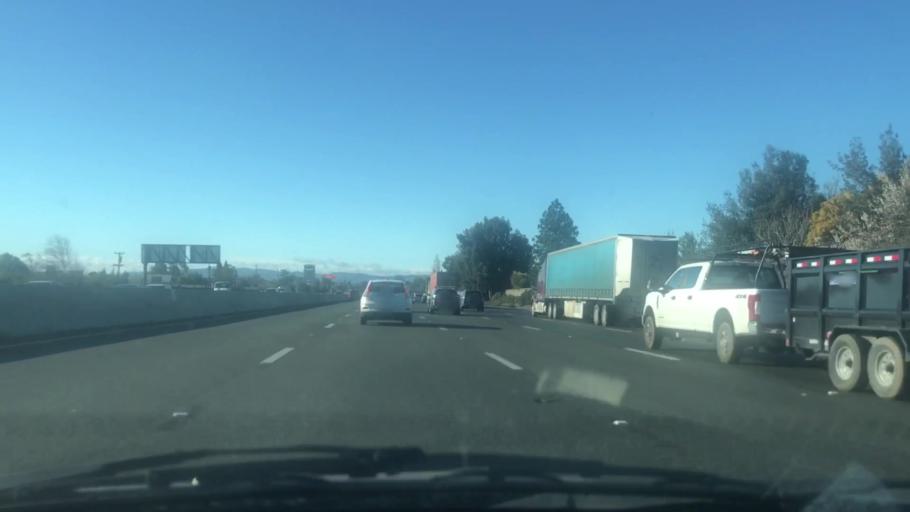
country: US
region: California
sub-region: Solano County
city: Fairfield
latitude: 38.2683
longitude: -122.0546
